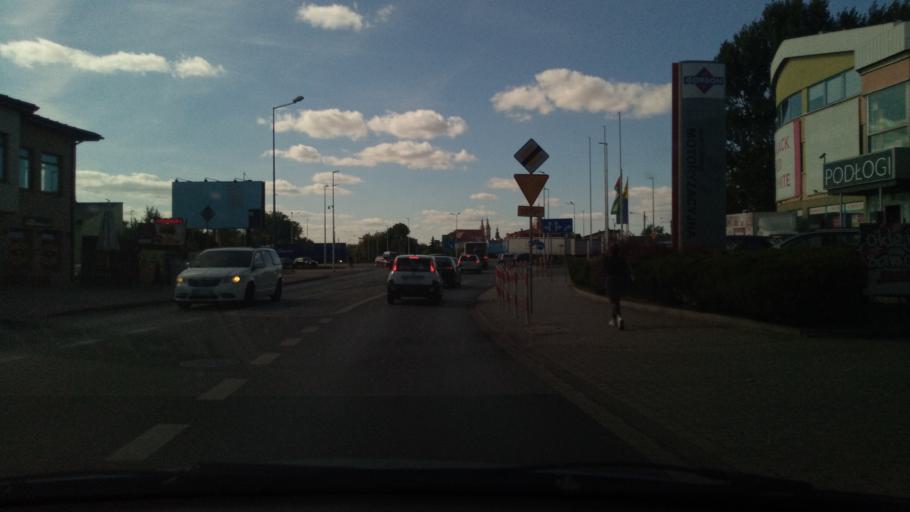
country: PL
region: Lodz Voivodeship
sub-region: Piotrkow Trybunalski
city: Piotrkow Trybunalski
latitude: 51.4053
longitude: 19.7052
